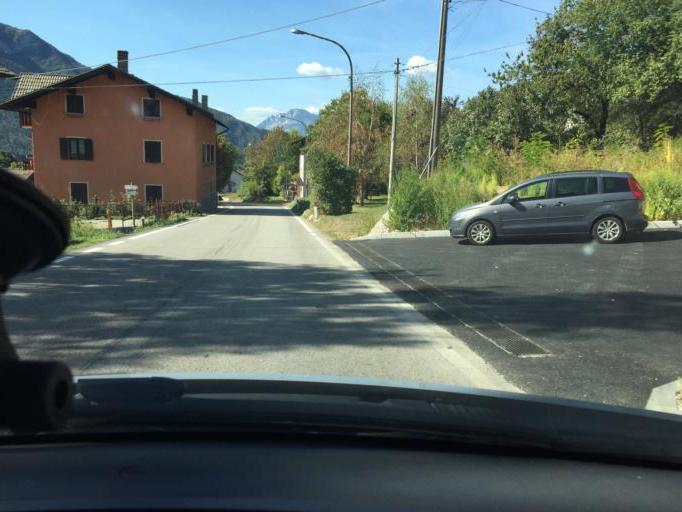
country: IT
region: Trentino-Alto Adige
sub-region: Provincia di Trento
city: Folgaria
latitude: 45.9129
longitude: 11.1574
